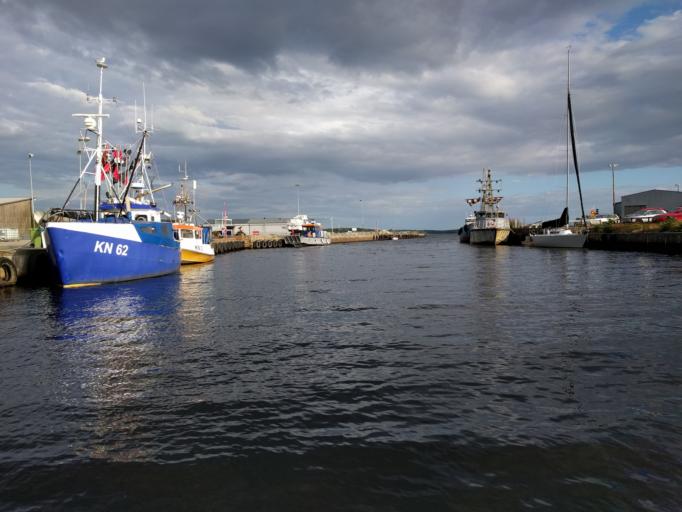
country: SE
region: Blekinge
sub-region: Ronneby Kommun
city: Ronneby
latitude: 56.1765
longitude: 15.3006
